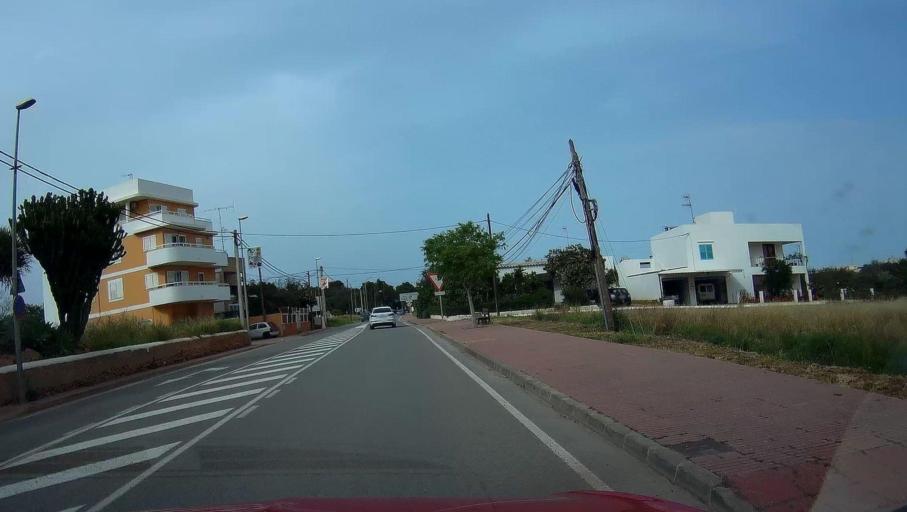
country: ES
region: Balearic Islands
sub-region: Illes Balears
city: Santa Eularia des Riu
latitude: 38.9885
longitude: 1.5393
